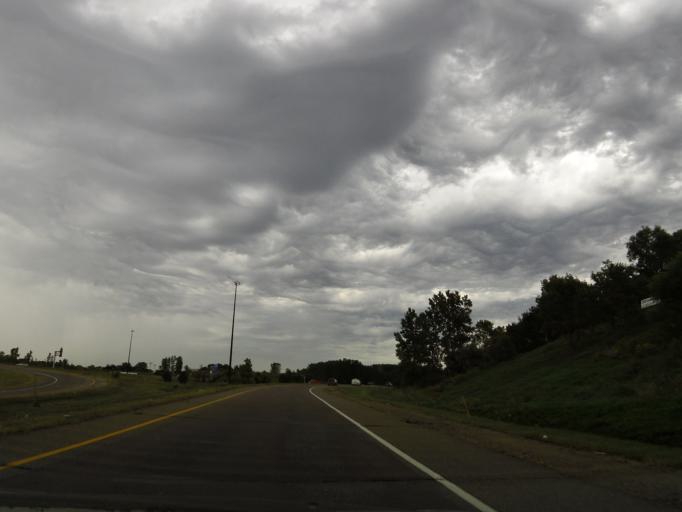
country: US
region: Minnesota
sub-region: Dakota County
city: Mendota Heights
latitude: 44.8609
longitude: -93.1437
